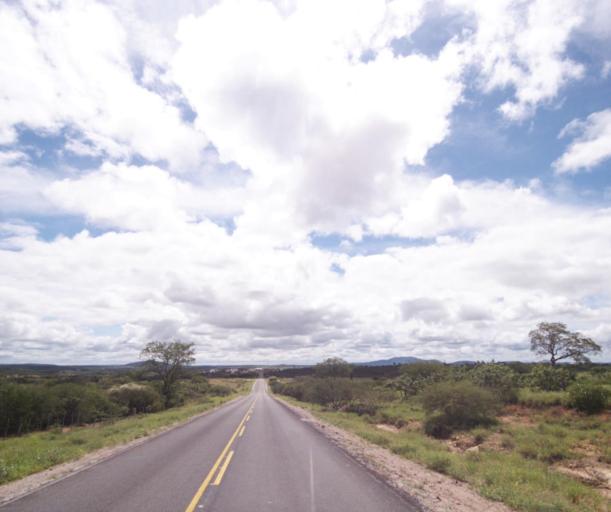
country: BR
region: Bahia
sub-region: Tanhacu
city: Tanhacu
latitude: -14.1592
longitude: -41.2276
